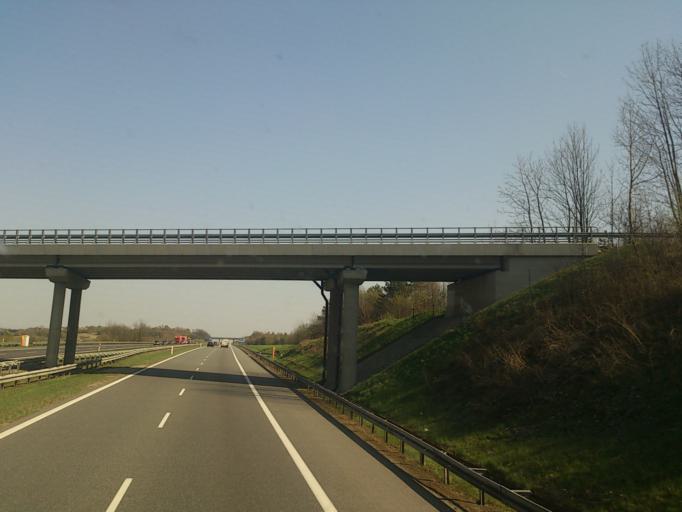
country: PL
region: Lesser Poland Voivodeship
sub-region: Powiat krakowski
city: Czulow
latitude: 50.0906
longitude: 19.6872
